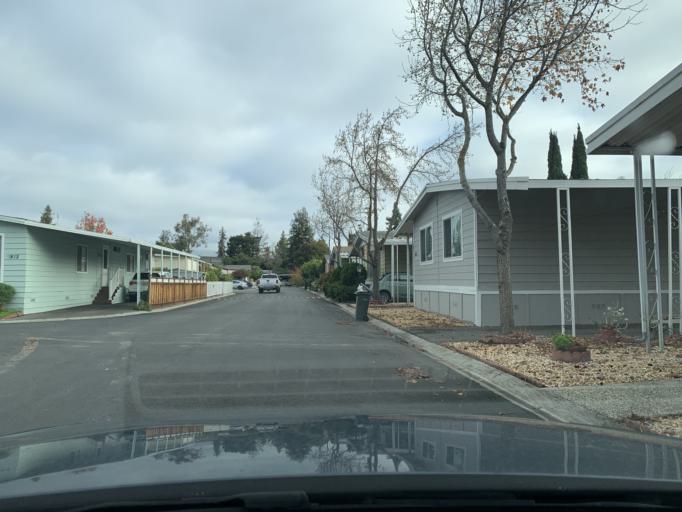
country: US
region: California
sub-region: Santa Clara County
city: Alum Rock
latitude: 37.3328
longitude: -121.8484
